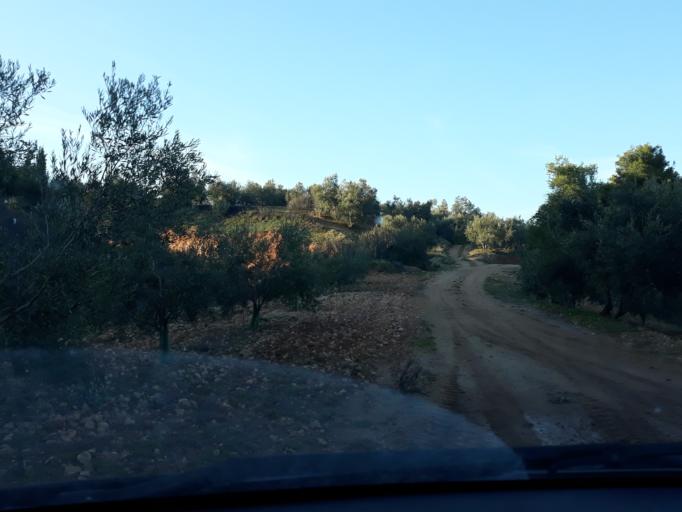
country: GR
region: Central Greece
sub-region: Nomos Voiotias
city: Asopia
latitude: 38.2744
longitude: 23.5297
